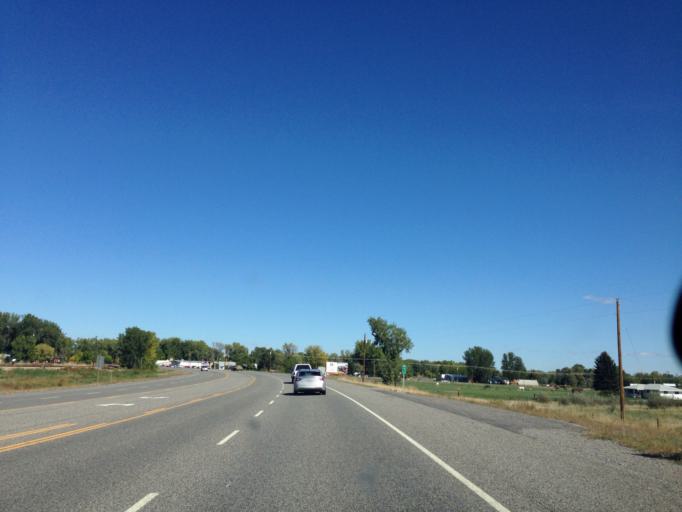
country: US
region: Montana
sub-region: Yellowstone County
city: Laurel
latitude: 45.6468
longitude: -108.7568
